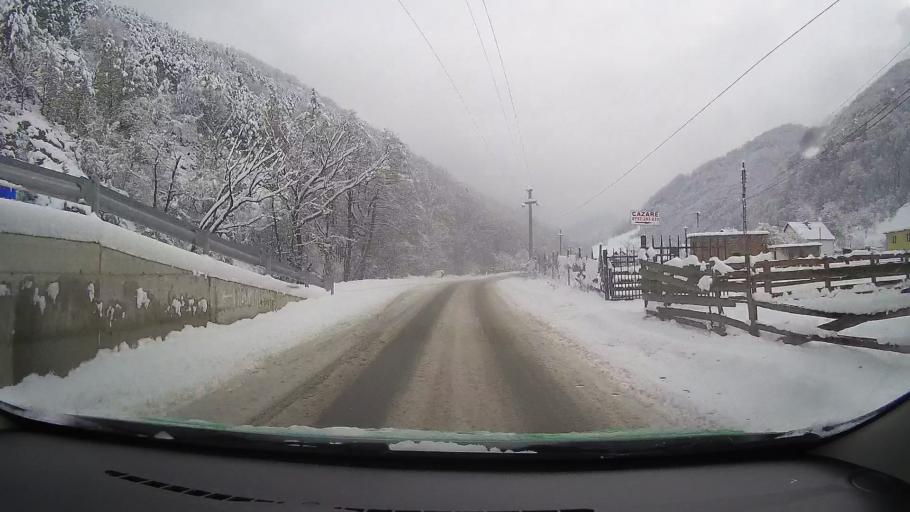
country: RO
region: Alba
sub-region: Comuna Sugag
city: Dobra
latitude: 45.7671
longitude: 23.6458
